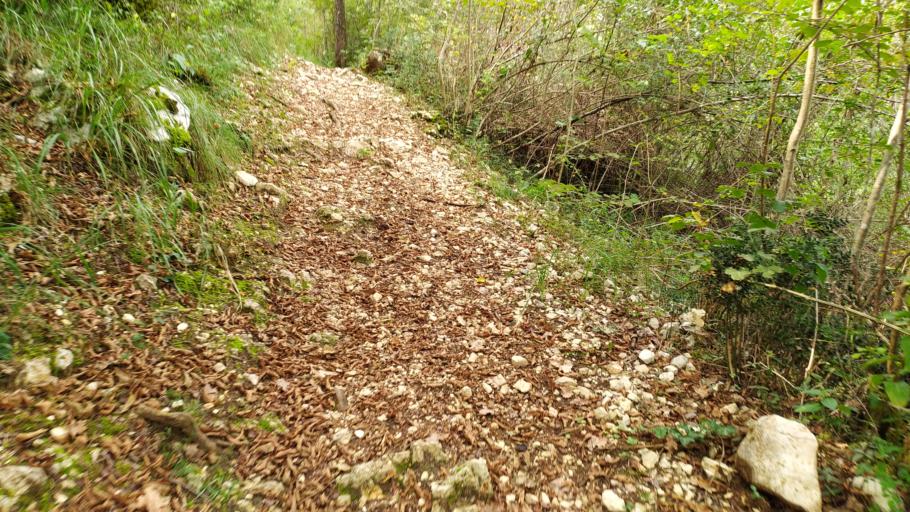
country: IT
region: Friuli Venezia Giulia
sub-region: Provincia di Pordenone
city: Aviano-Castello
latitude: 46.0780
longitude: 12.5741
